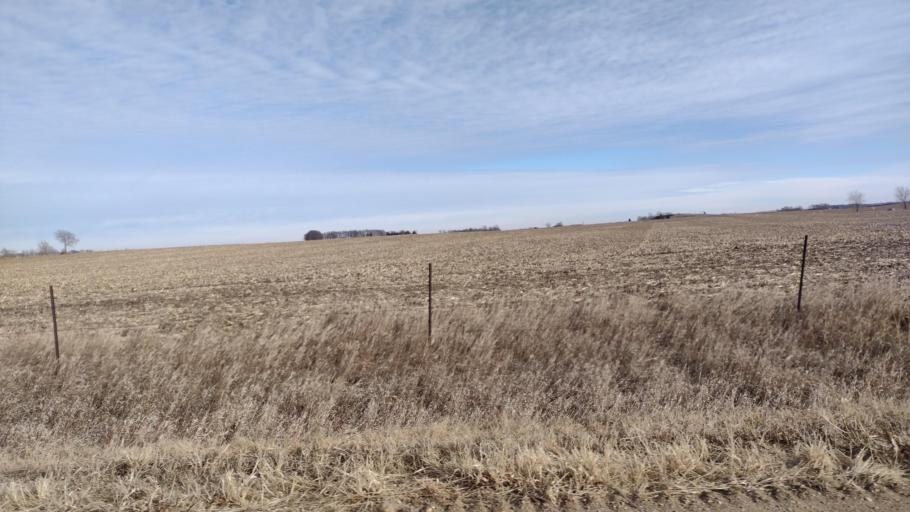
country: US
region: South Dakota
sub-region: Union County
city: Beresford
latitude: 42.9560
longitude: -96.8055
